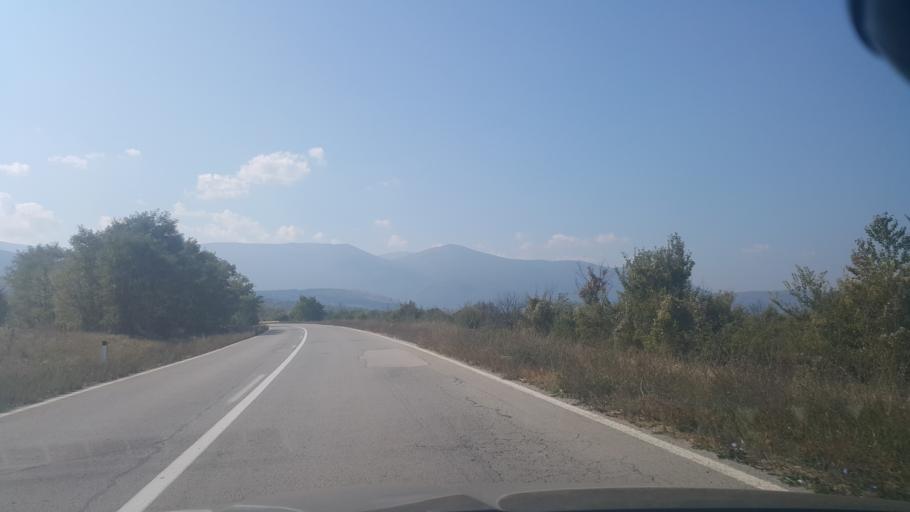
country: RS
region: Central Serbia
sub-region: Pirotski Okrug
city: Bela Palanka
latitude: 43.2266
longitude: 22.3718
